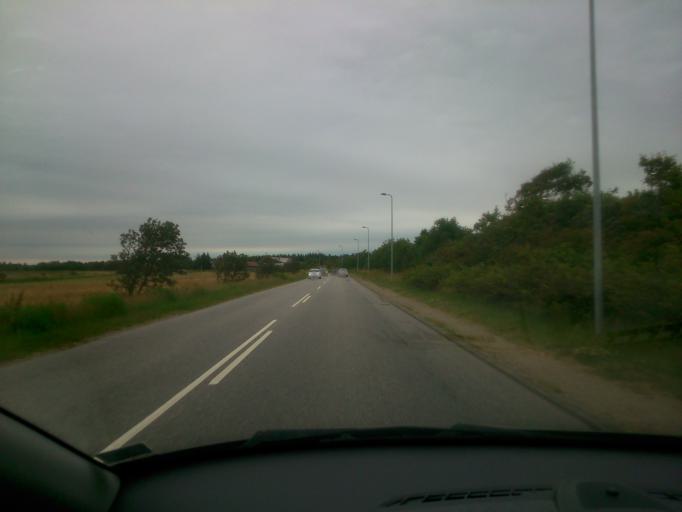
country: DK
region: Central Jutland
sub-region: Ringkobing-Skjern Kommune
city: Skjern
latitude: 55.9488
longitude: 8.4824
